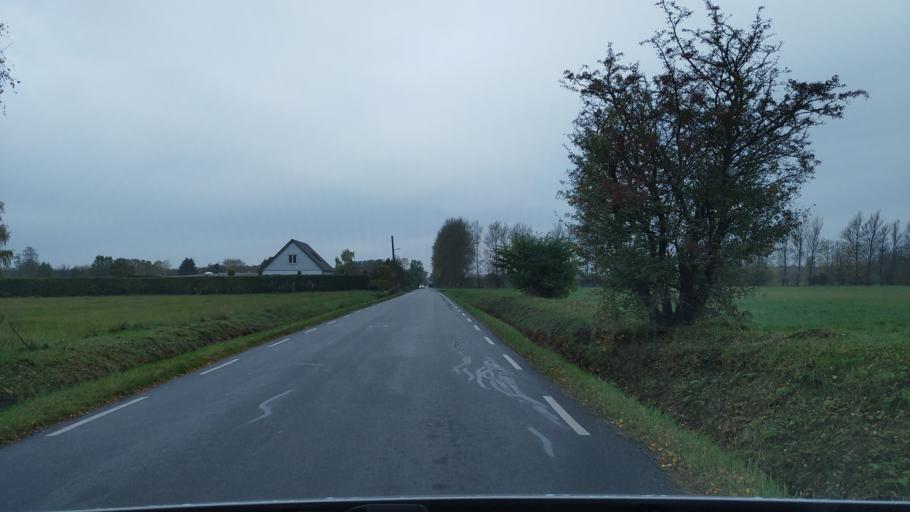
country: DK
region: Capital Region
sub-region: Tarnby Kommune
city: Tarnby
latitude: 55.5742
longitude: 12.6069
